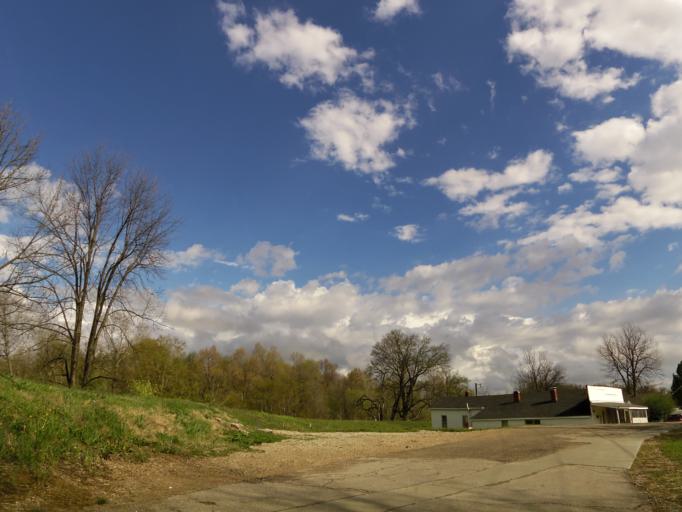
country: US
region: Missouri
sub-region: Butler County
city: Poplar Bluff
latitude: 36.7614
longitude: -90.3856
